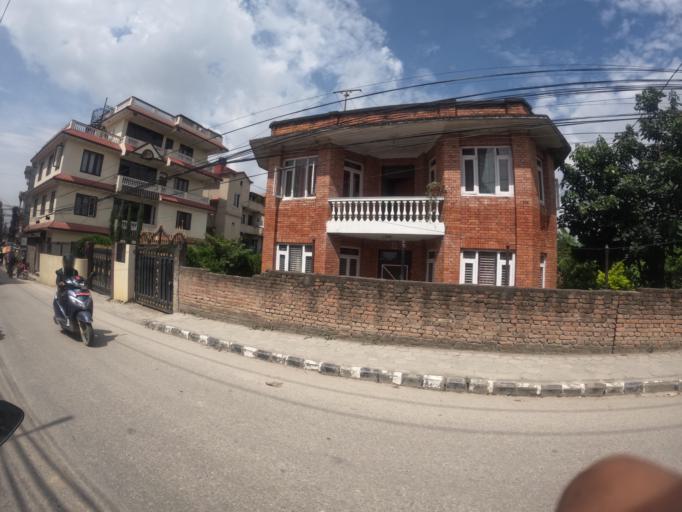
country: NP
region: Central Region
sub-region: Bagmati Zone
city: Kathmandu
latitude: 27.6810
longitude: 85.3663
